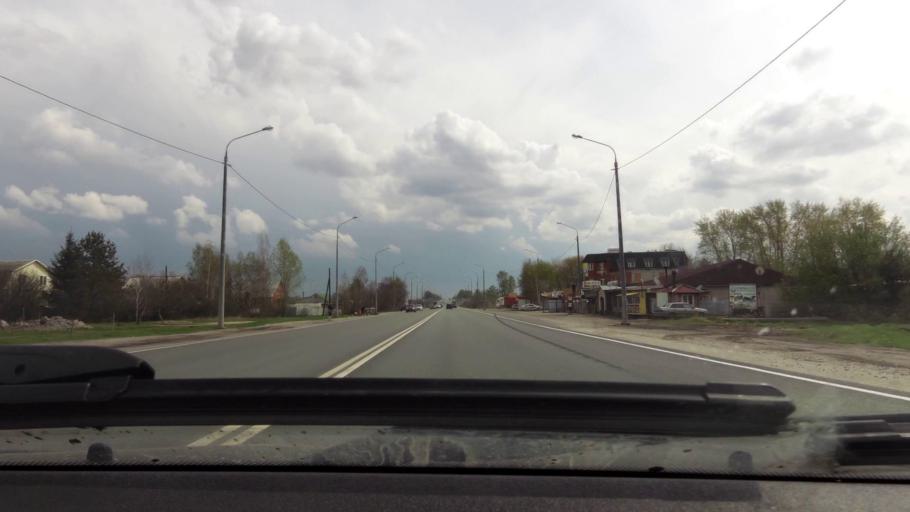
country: RU
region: Rjazan
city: Bagramovo
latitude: 54.7327
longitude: 39.4591
